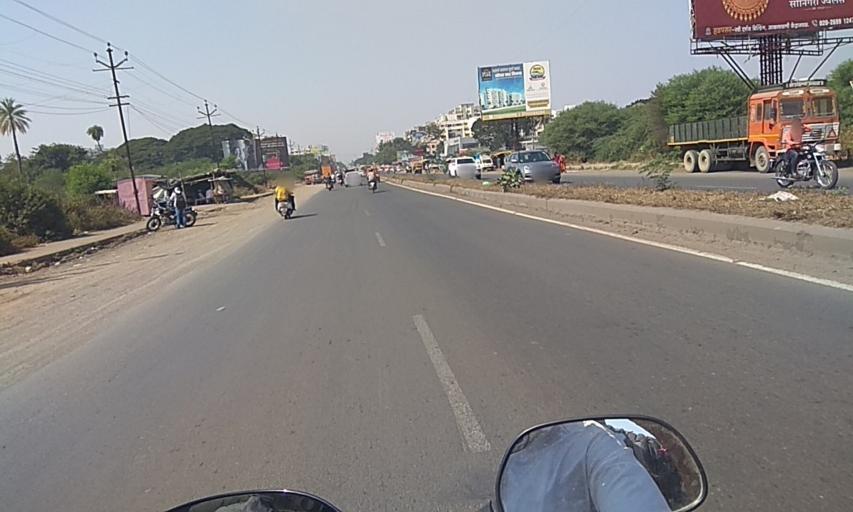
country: IN
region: Maharashtra
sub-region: Pune Division
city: Lohogaon
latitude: 18.4970
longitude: 73.9658
